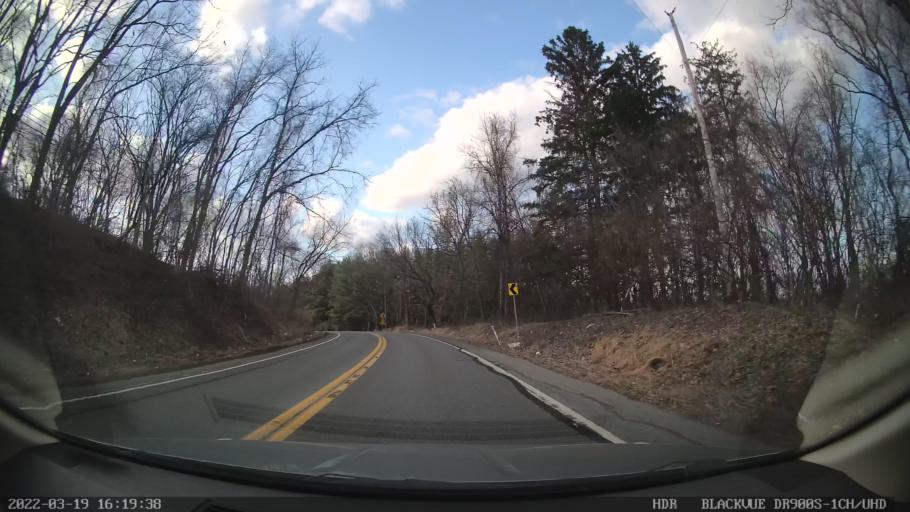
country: US
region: Pennsylvania
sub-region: Lehigh County
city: Dorneyville
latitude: 40.5728
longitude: -75.4990
